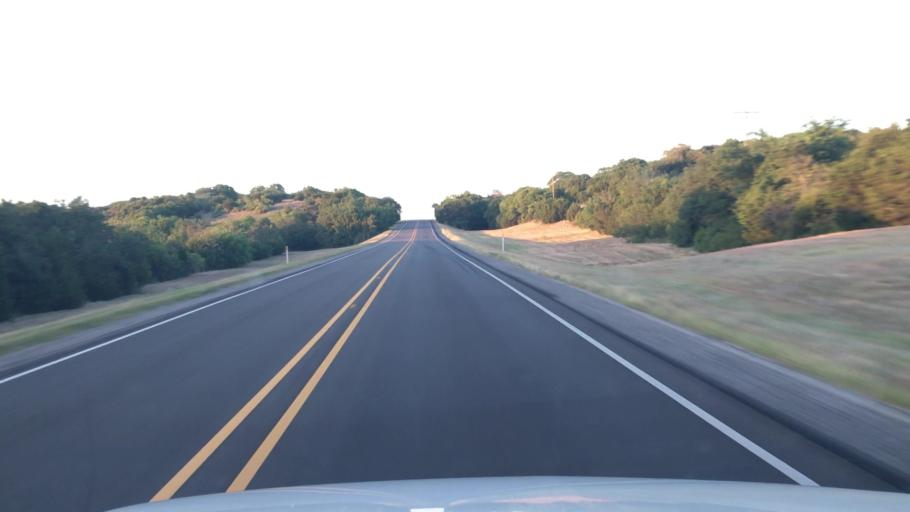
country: US
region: Texas
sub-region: Hamilton County
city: Hico
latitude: 32.0970
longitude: -97.9663
